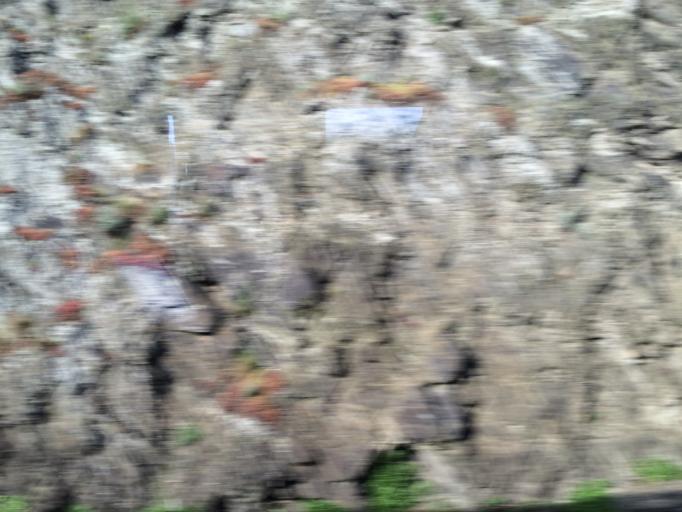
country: DE
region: Rheinland-Pfalz
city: Oberwesel
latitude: 50.1069
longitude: 7.7362
